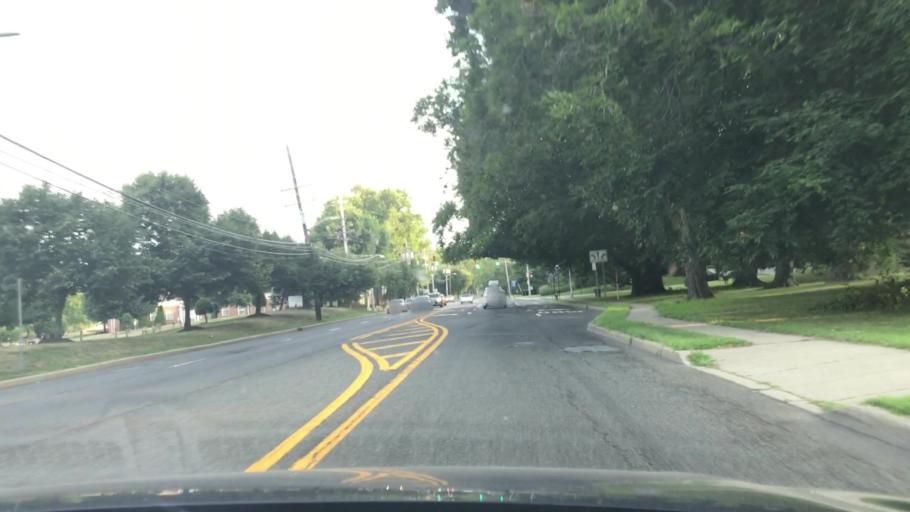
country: US
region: New Jersey
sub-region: Bergen County
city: Oradell
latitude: 40.9613
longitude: -74.0308
